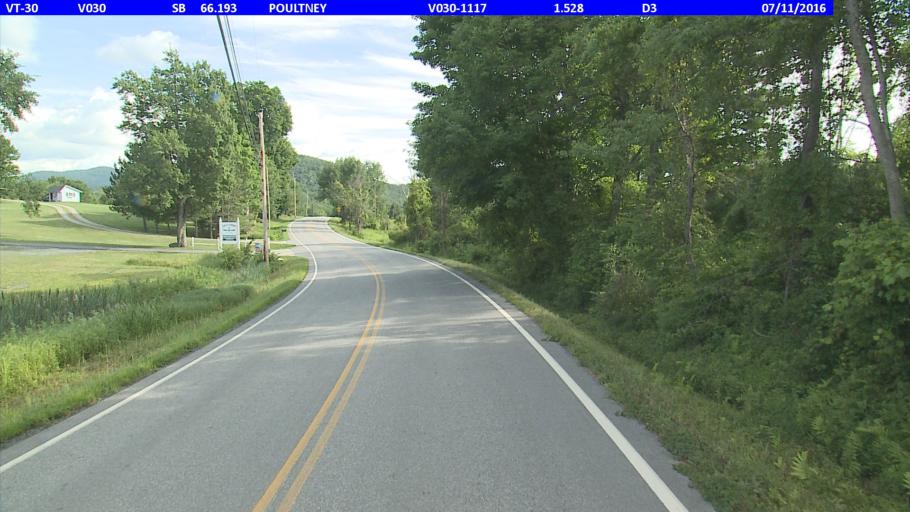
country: US
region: Vermont
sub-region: Rutland County
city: Poultney
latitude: 43.4854
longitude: -73.2032
